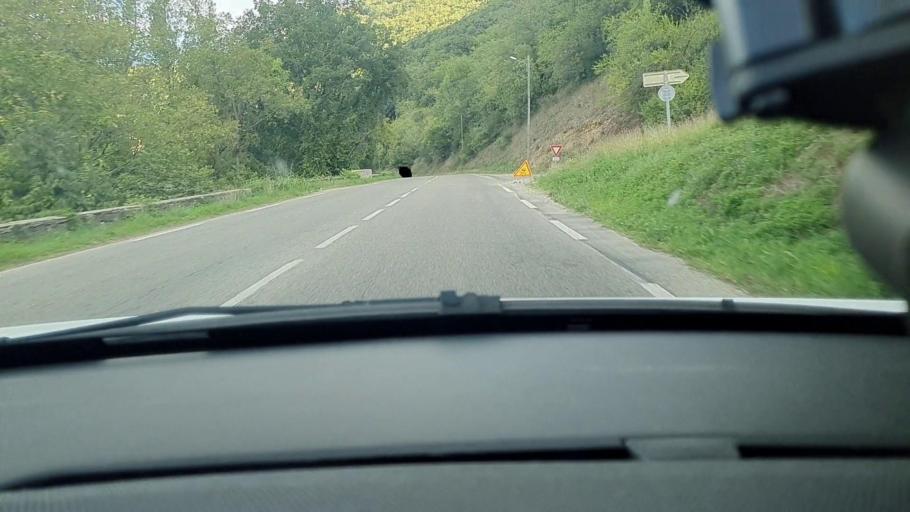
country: FR
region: Languedoc-Roussillon
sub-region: Departement du Gard
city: Molieres-sur-Ceze
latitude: 44.2742
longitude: 4.1521
